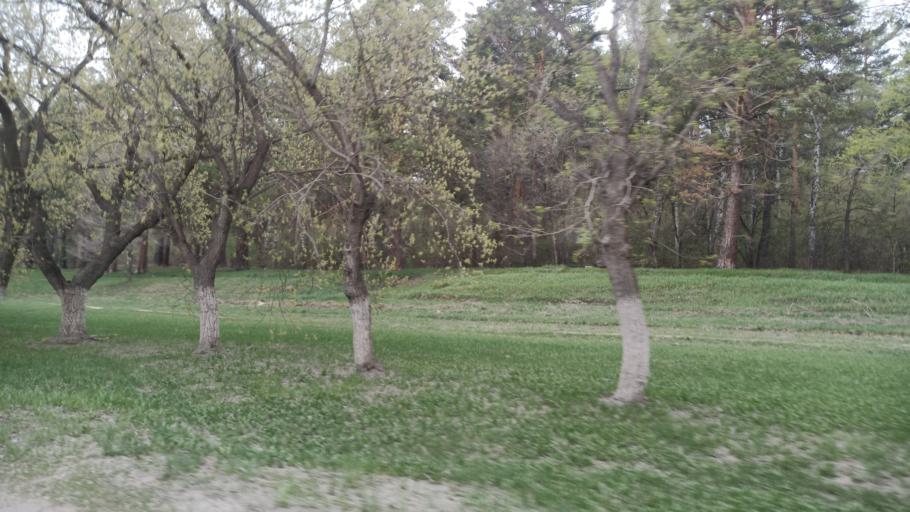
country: RU
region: Altai Krai
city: Yuzhnyy
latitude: 53.2593
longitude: 83.6957
